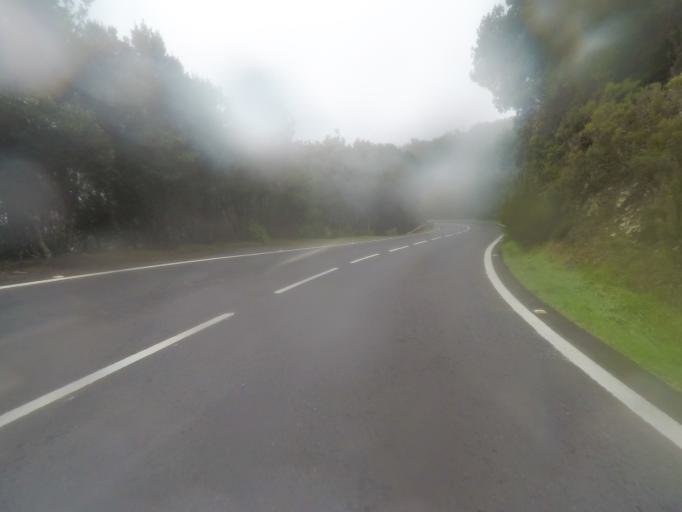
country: ES
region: Canary Islands
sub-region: Provincia de Santa Cruz de Tenerife
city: Vallehermosa
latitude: 28.1269
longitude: -17.2628
